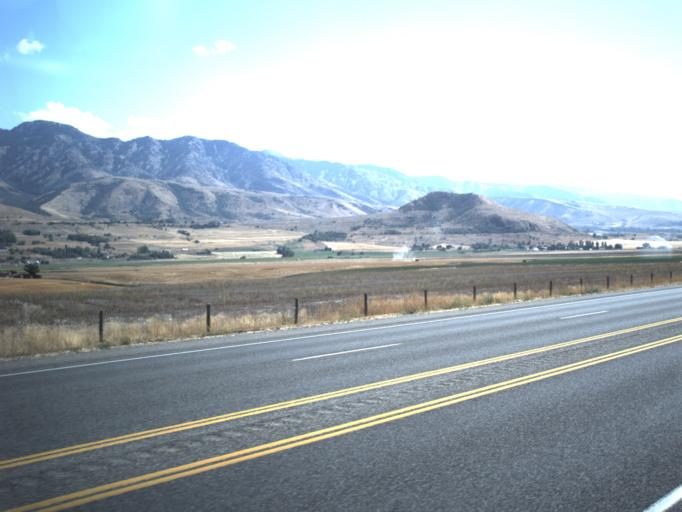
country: US
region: Utah
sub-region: Cache County
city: Lewiston
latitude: 41.9925
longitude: -111.8129
